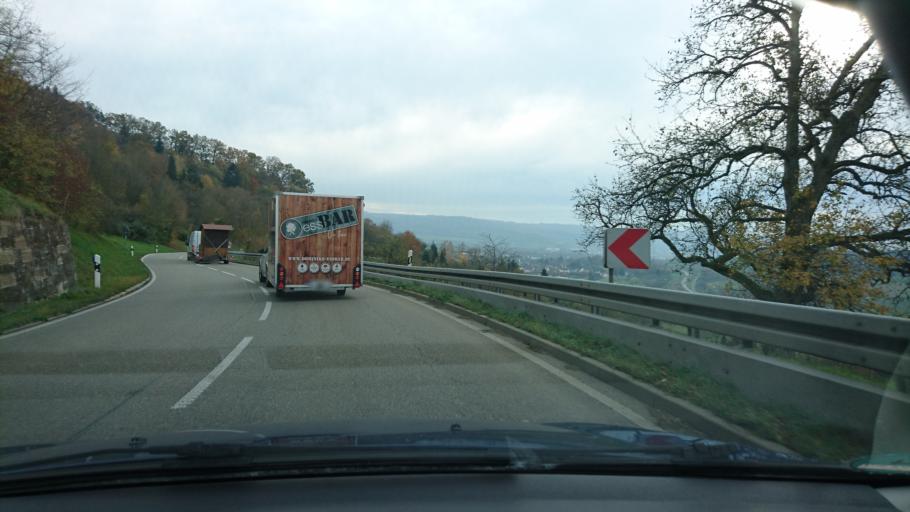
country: DE
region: Baden-Wuerttemberg
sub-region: Regierungsbezirk Stuttgart
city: Urbach
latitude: 48.8411
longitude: 9.5475
